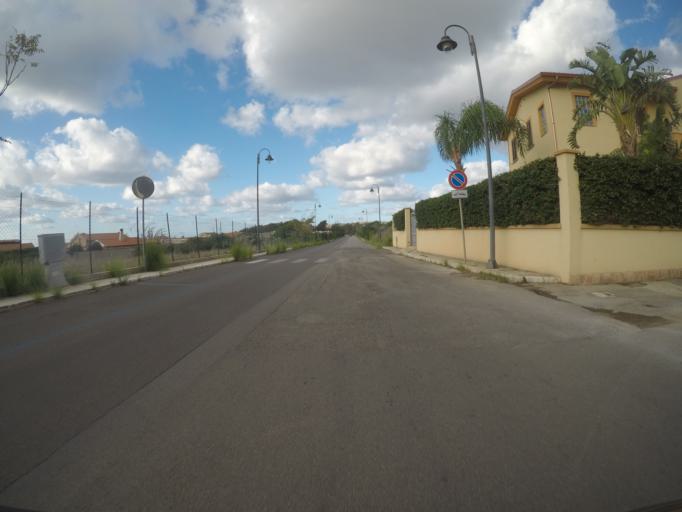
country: IT
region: Sicily
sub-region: Palermo
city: Isola delle Femmine
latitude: 38.1902
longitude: 13.2451
